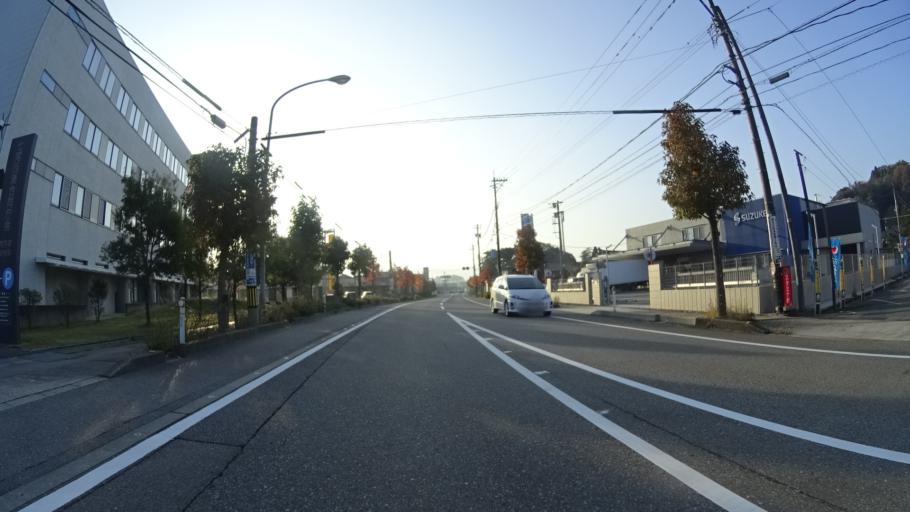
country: JP
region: Ishikawa
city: Nanao
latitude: 37.0552
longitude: 136.9544
